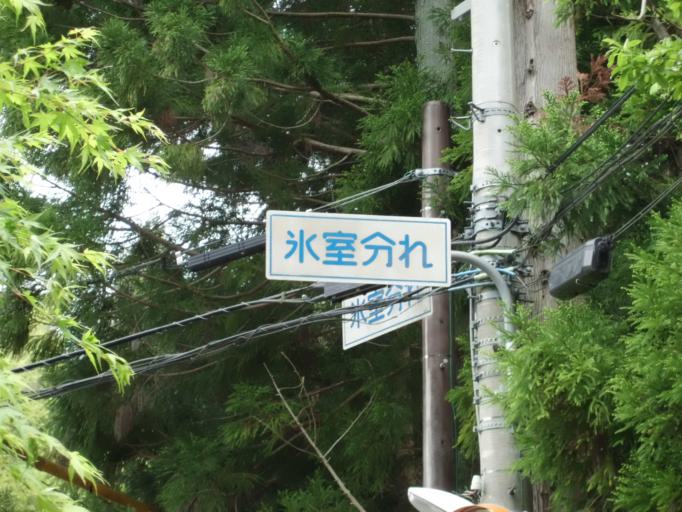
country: JP
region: Kyoto
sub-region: Kyoto-shi
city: Kamigyo-ku
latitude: 35.0733
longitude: 135.7174
